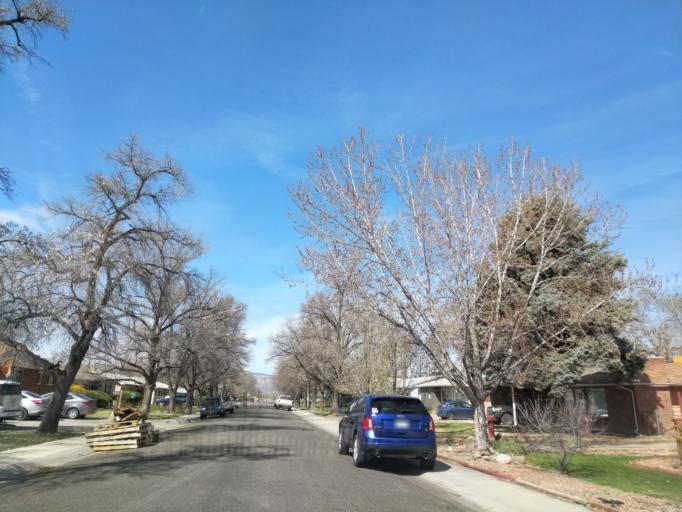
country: US
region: Colorado
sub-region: Mesa County
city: Grand Junction
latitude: 39.0829
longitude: -108.5689
